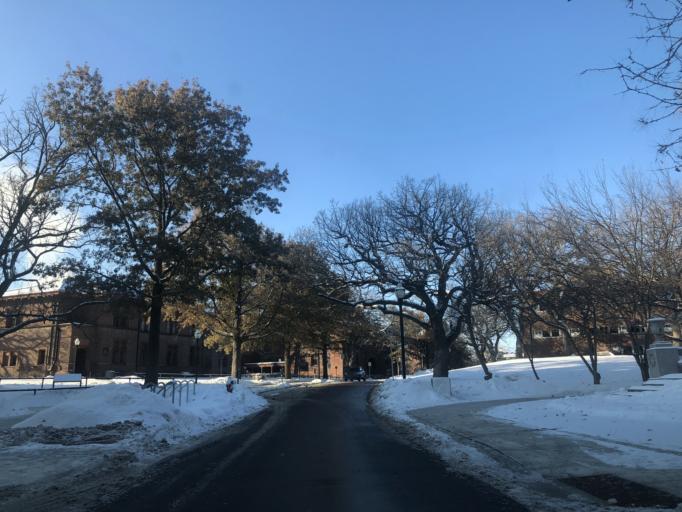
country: US
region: Minnesota
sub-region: Hennepin County
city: Minneapolis
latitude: 44.9781
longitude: -93.2369
